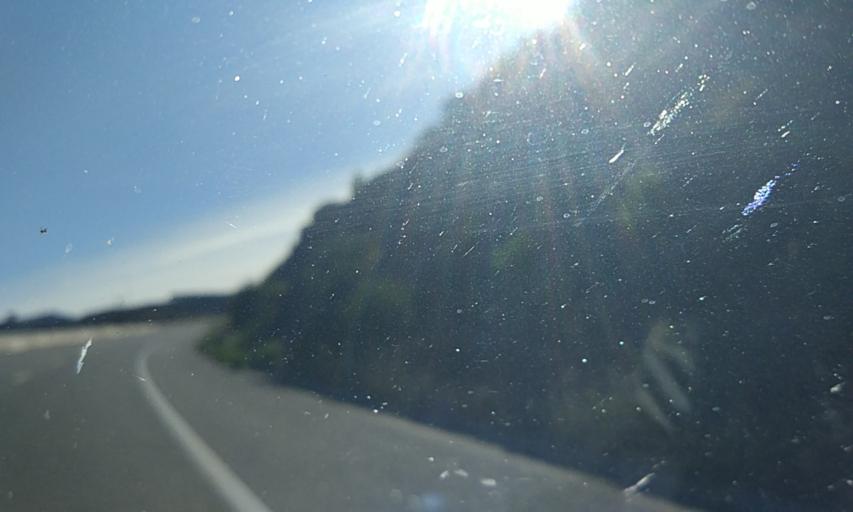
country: PT
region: Vila Real
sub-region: Murca
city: Murca
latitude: 41.4030
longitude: -7.4544
